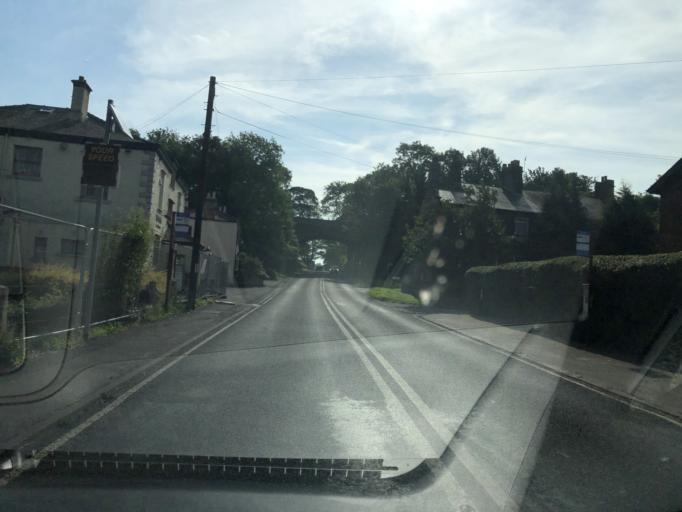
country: GB
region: England
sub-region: City and Borough of Leeds
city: Pool
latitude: 53.8993
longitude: -1.6073
